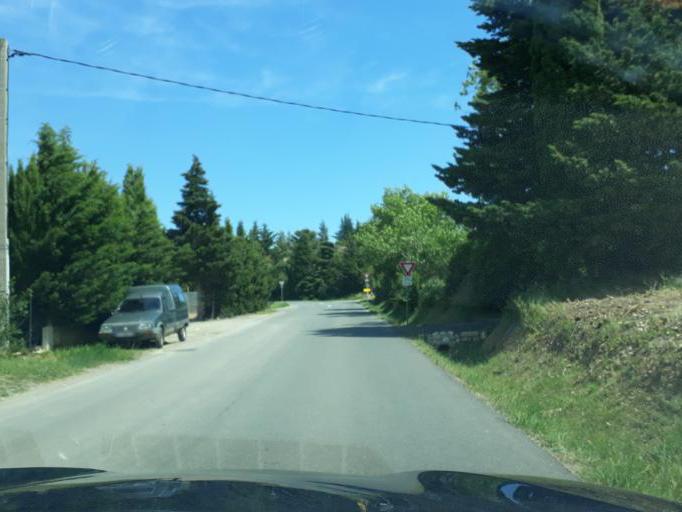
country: FR
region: Languedoc-Roussillon
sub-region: Departement de l'Aude
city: Portel-des-Corbieres
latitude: 43.0479
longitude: 2.9239
